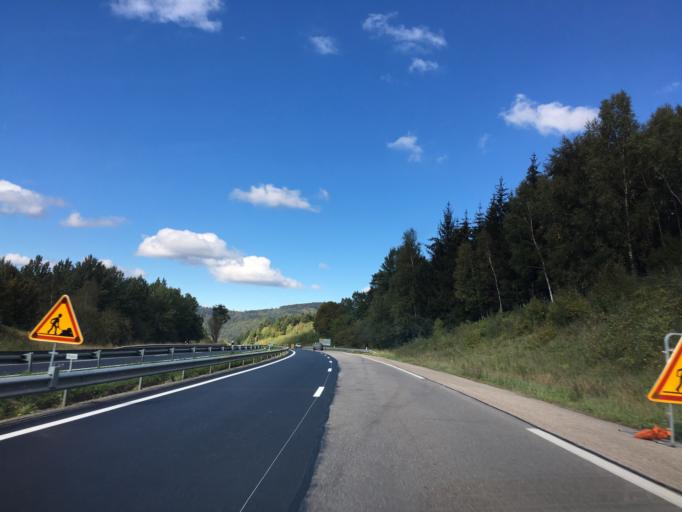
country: FR
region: Lorraine
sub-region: Departement des Vosges
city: Moyenmoutier
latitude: 48.3617
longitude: 6.8852
